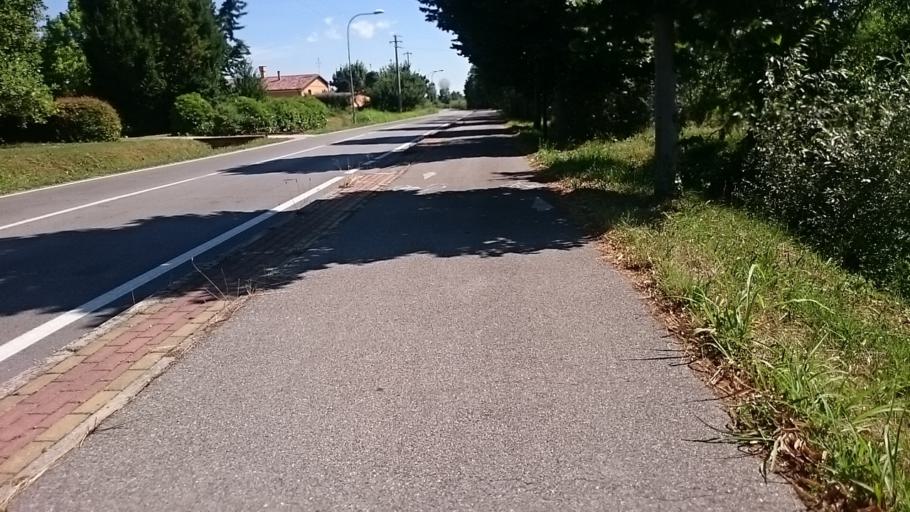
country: IT
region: Veneto
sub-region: Provincia di Venezia
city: Arino
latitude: 45.4323
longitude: 12.0519
